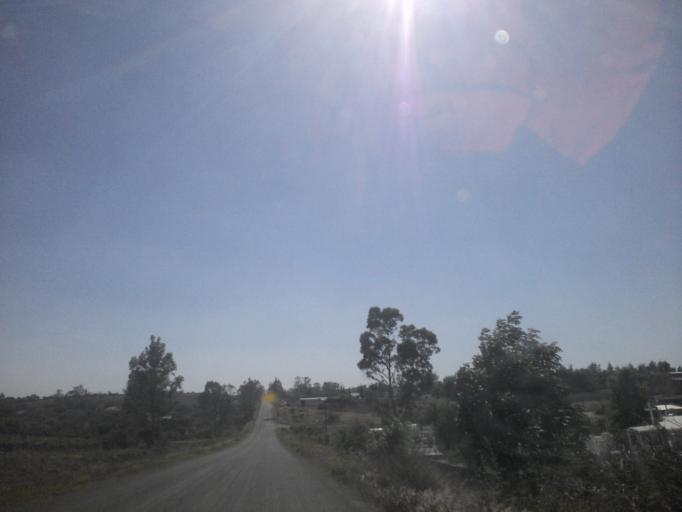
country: MX
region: Jalisco
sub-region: Arandas
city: Santiaguito (Santiaguito de Velazquez)
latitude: 20.8323
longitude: -102.1177
